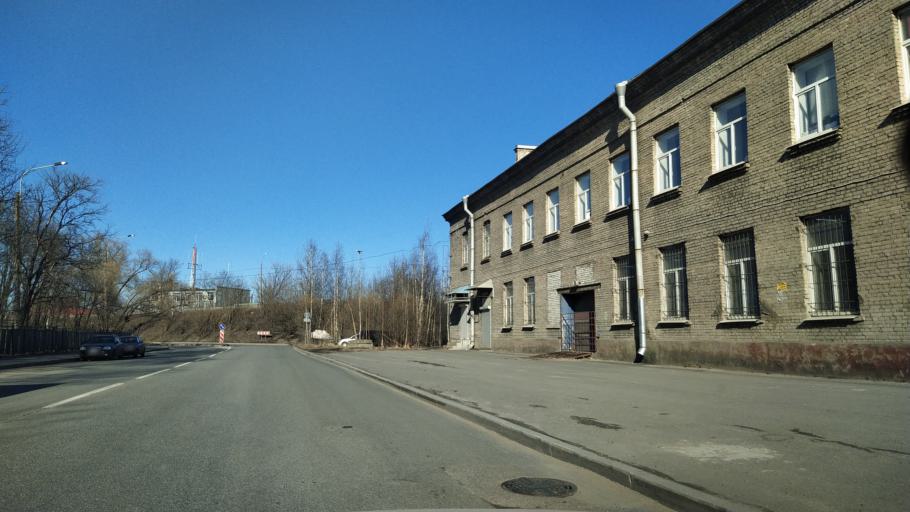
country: RU
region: St.-Petersburg
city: Centralniy
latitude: 59.9030
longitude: 30.3750
